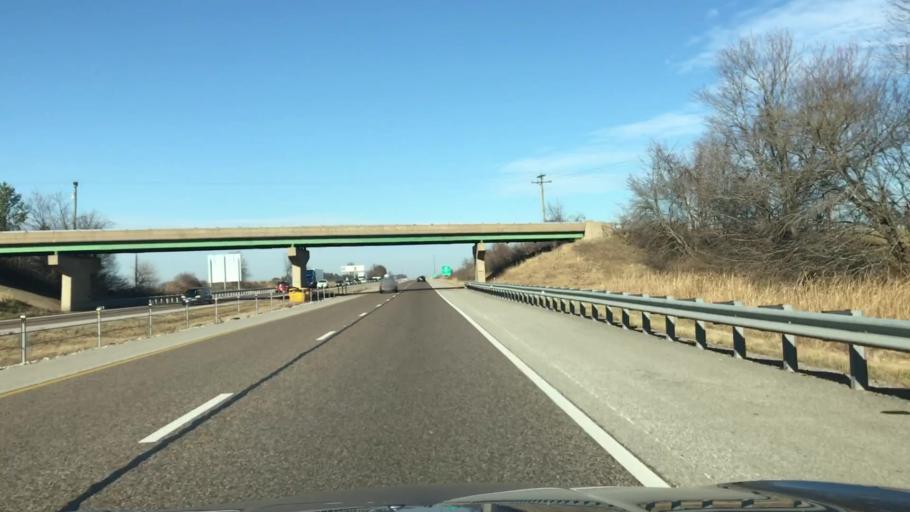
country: US
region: Illinois
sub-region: Madison County
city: Troy
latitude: 38.7820
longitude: -89.8989
